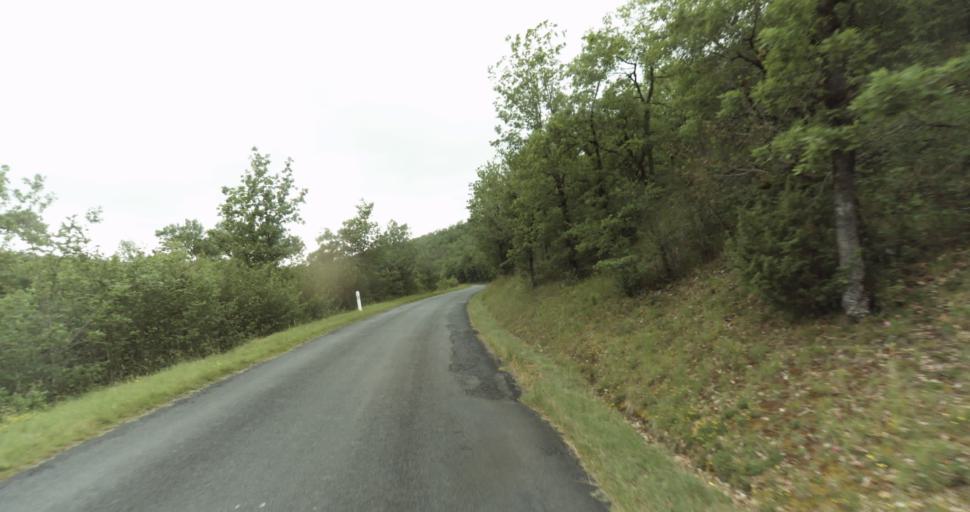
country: FR
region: Aquitaine
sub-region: Departement de la Dordogne
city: Beaumont-du-Perigord
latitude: 44.7536
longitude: 0.8173
